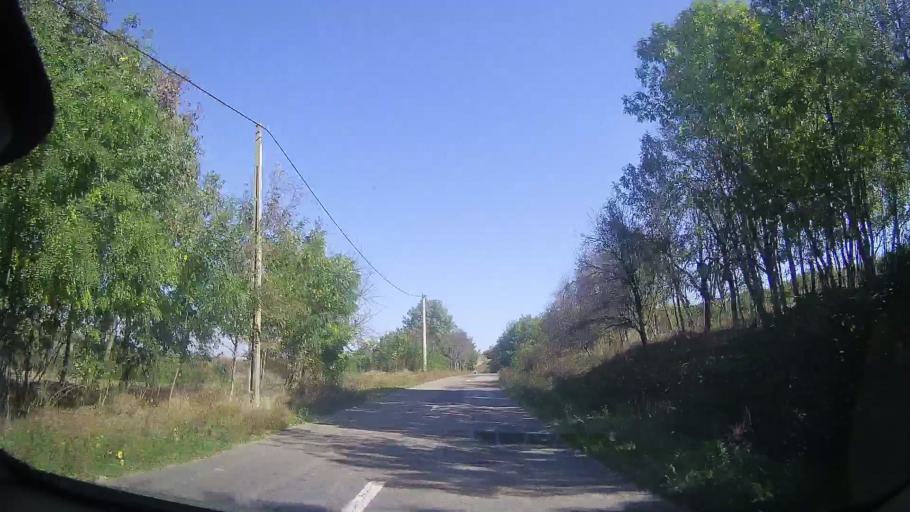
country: RO
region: Timis
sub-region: Comuna Bara
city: Bara
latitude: 45.9013
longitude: 21.8884
